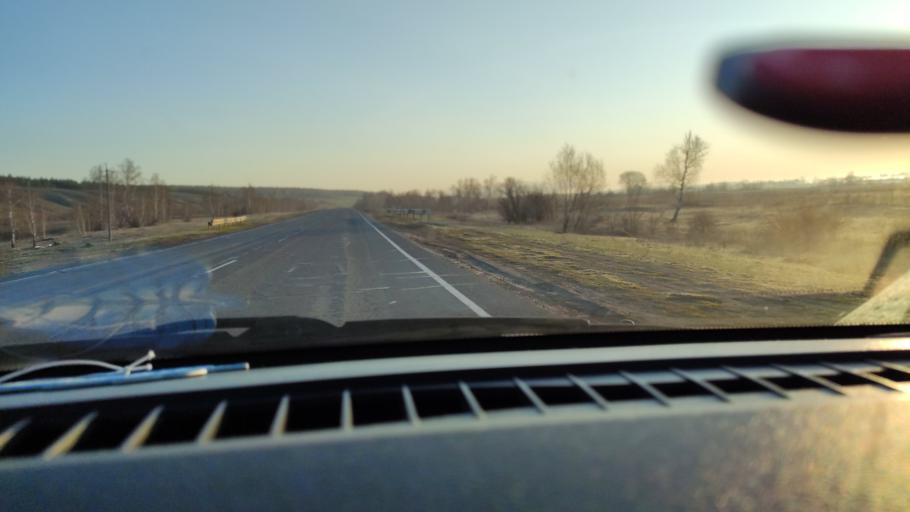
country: RU
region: Saratov
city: Sinodskoye
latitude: 52.0572
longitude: 46.7599
